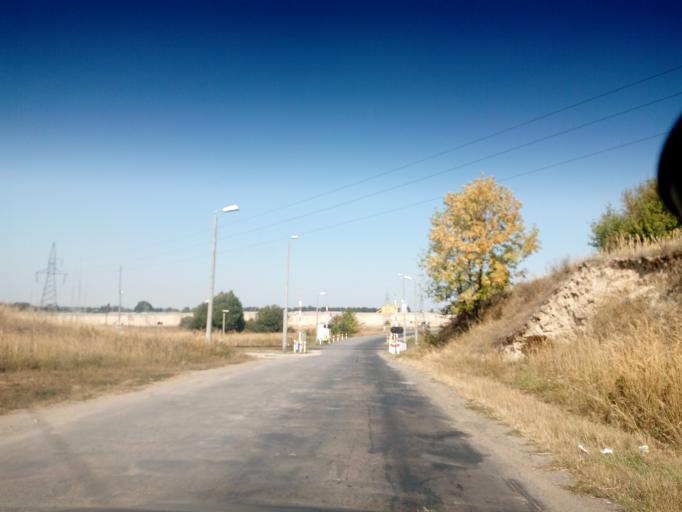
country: PL
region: Lublin Voivodeship
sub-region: Powiat hrubieszowski
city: Hrubieszow
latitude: 50.7856
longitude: 23.9012
